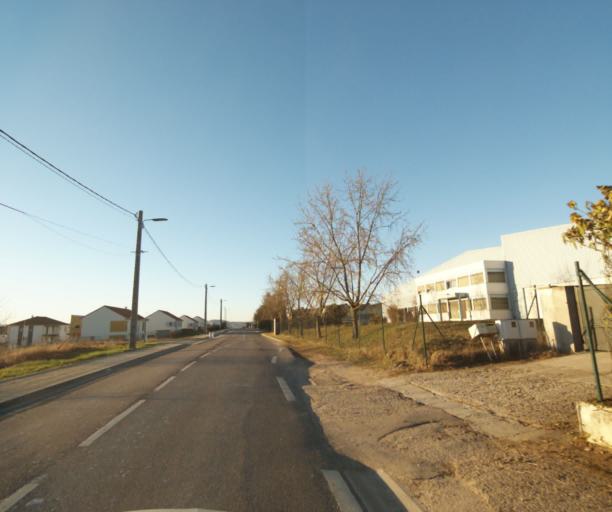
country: FR
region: Lorraine
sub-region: Departement de Meurthe-et-Moselle
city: Tomblaine
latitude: 48.6731
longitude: 6.2254
